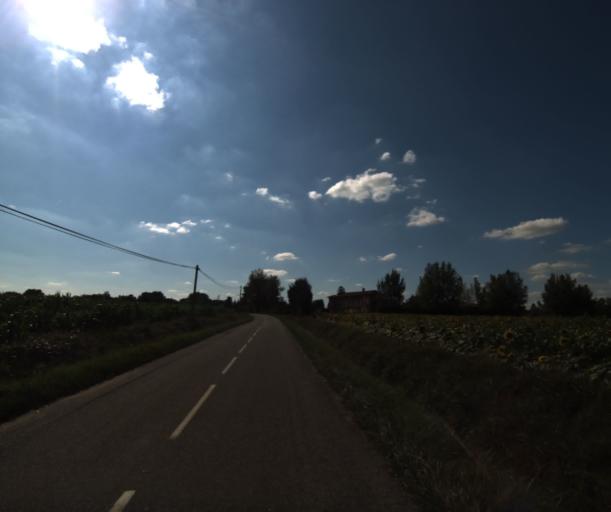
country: FR
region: Midi-Pyrenees
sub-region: Departement de la Haute-Garonne
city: Fonsorbes
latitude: 43.5031
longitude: 1.2115
